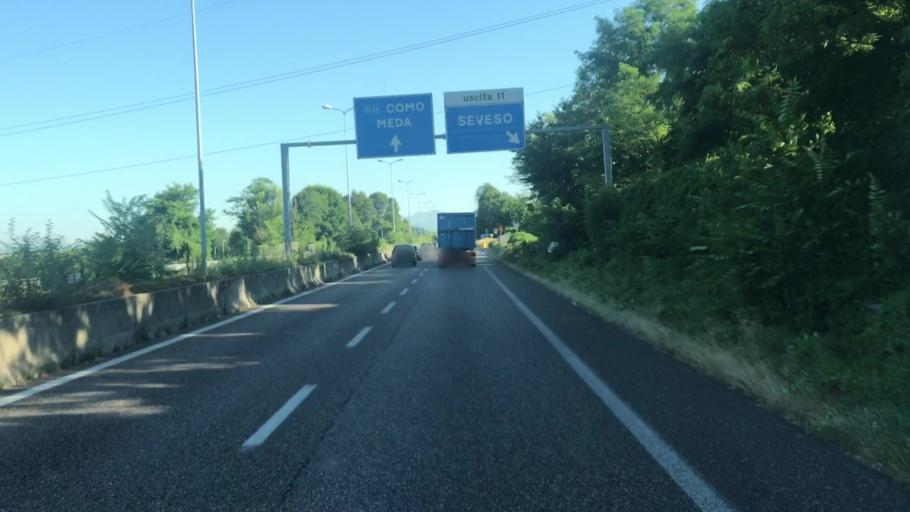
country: IT
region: Lombardy
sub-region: Provincia di Monza e Brianza
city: Cesano Maderno
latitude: 45.6363
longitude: 9.1599
